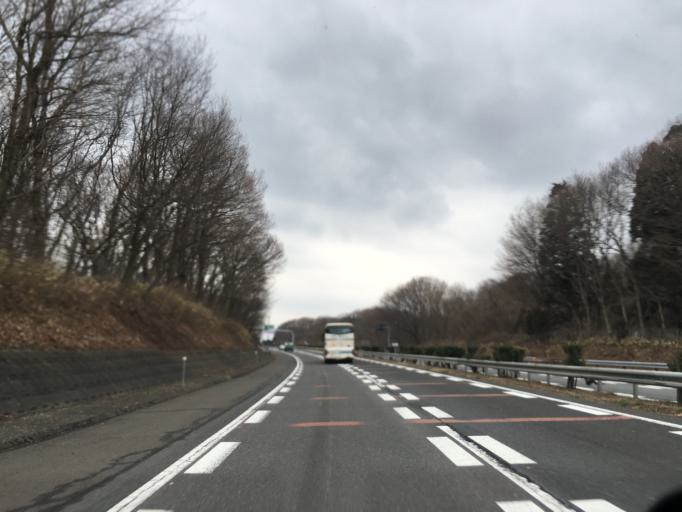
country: JP
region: Tochigi
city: Kuroiso
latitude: 37.0775
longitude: 140.1197
